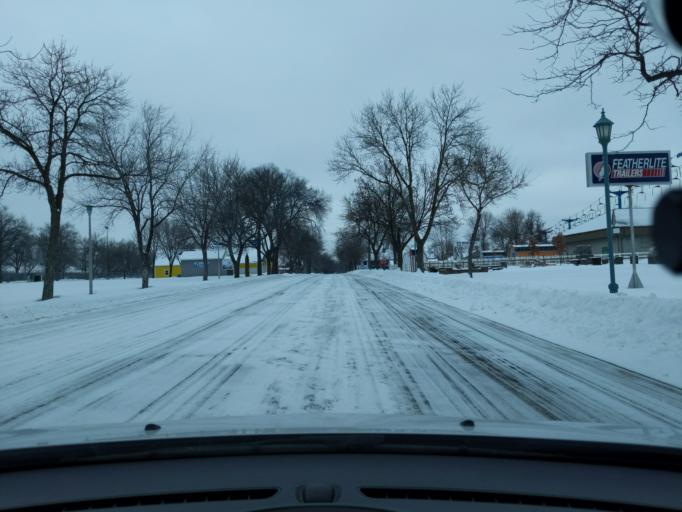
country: US
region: Minnesota
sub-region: Ramsey County
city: Falcon Heights
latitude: 44.9847
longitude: -93.1705
